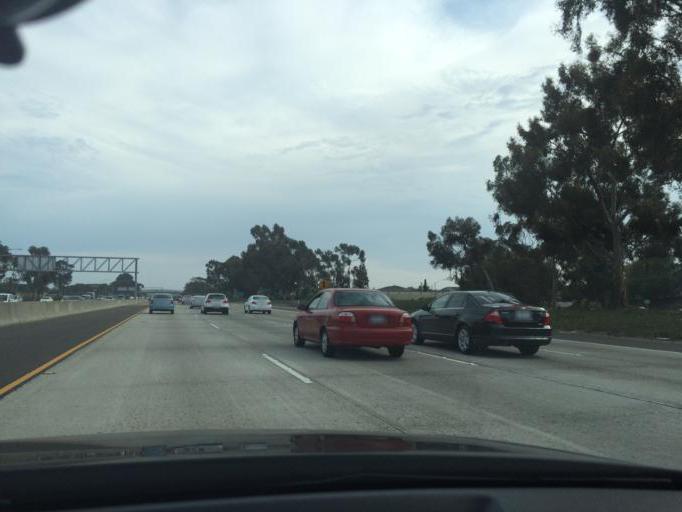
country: US
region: California
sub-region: San Diego County
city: San Diego
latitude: 32.7929
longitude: -117.1587
